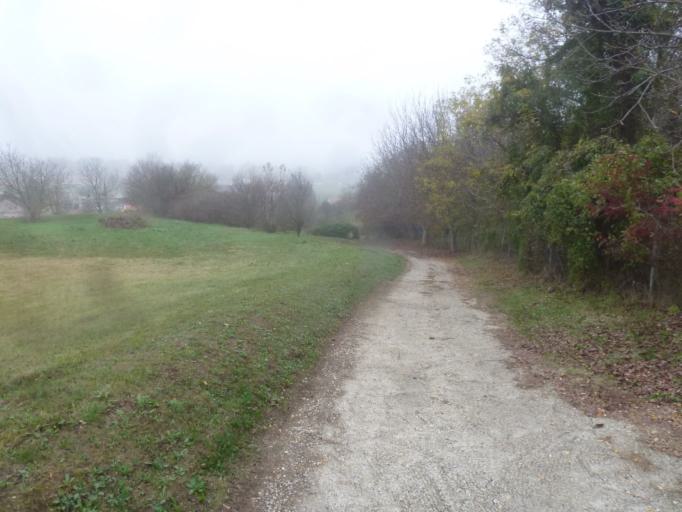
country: HU
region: Zala
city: Nagykanizsa
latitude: 46.5425
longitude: 16.9885
